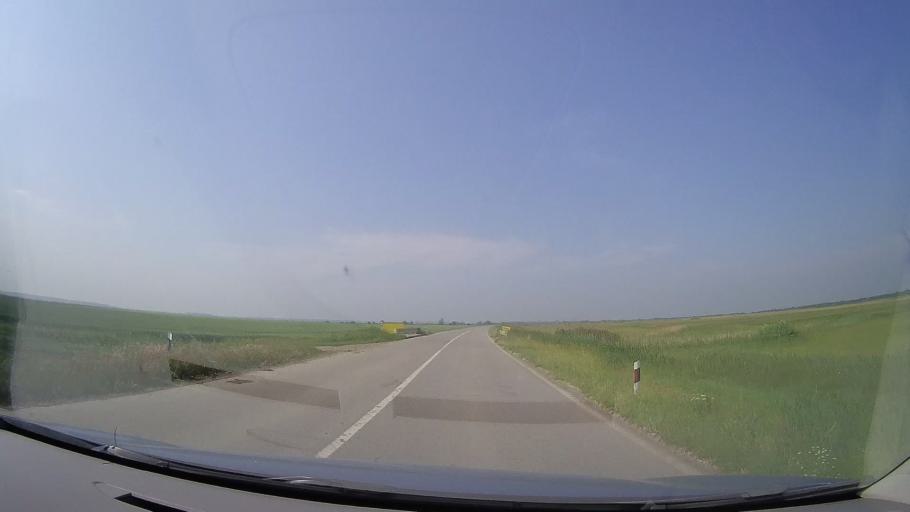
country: RS
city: Jasa Tomic
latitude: 45.4122
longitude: 20.8288
